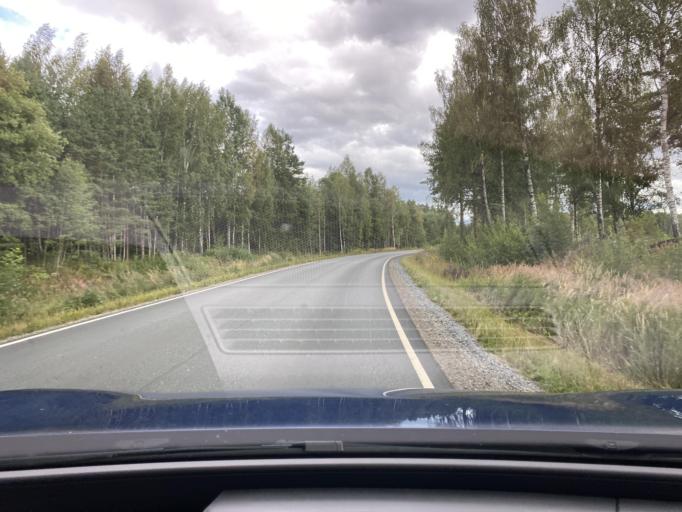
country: FI
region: Pirkanmaa
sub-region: Lounais-Pirkanmaa
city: Vammala
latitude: 61.3018
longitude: 22.9543
